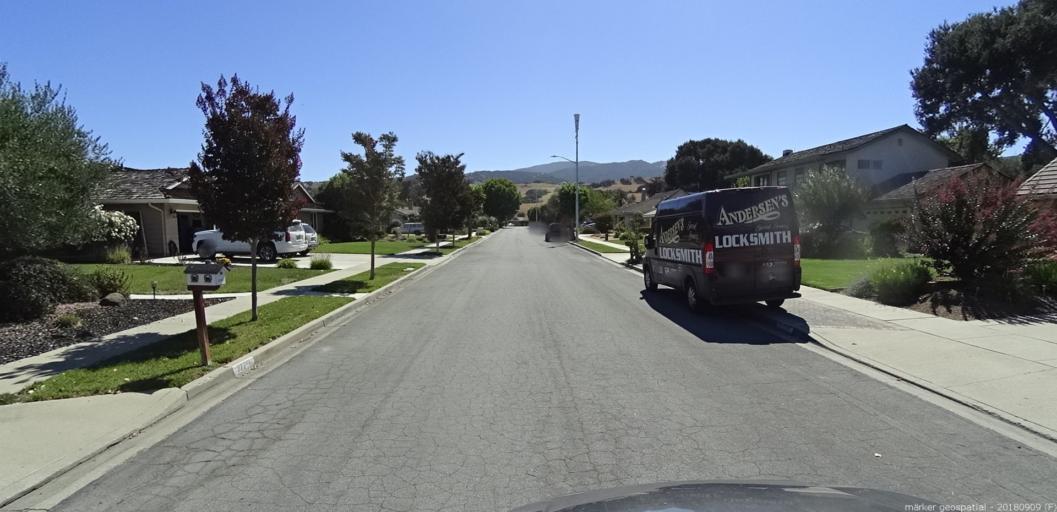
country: US
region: California
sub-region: Monterey County
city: Salinas
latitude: 36.5999
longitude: -121.7023
